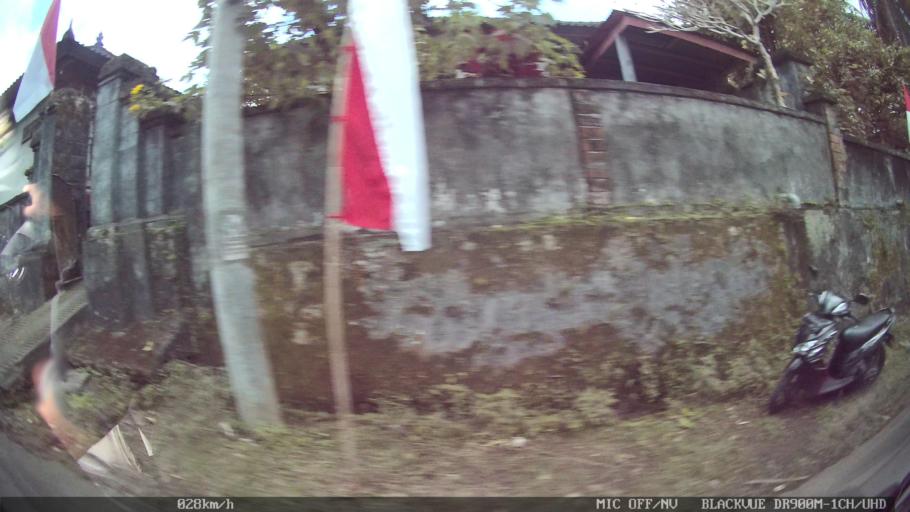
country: ID
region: Bali
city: Banjar Petak
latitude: -8.4396
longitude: 115.3235
